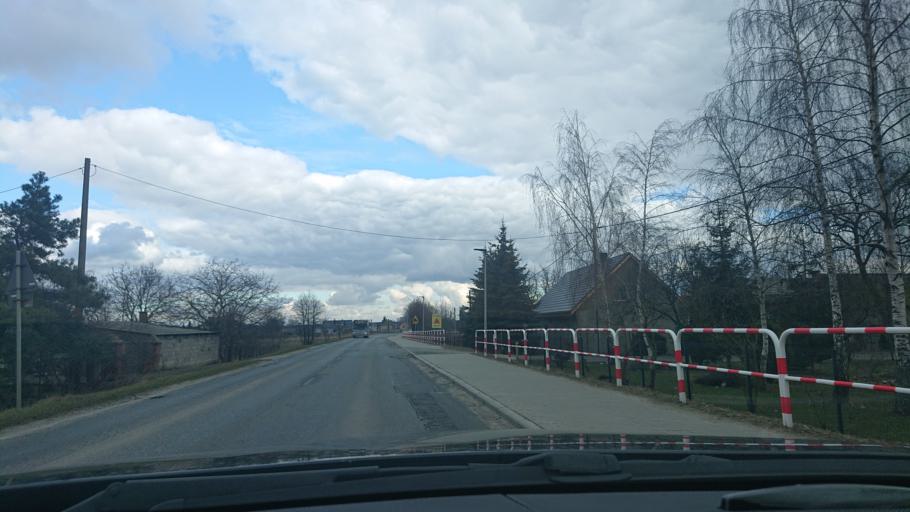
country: PL
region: Greater Poland Voivodeship
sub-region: Powiat gnieznienski
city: Niechanowo
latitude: 52.5500
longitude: 17.6805
